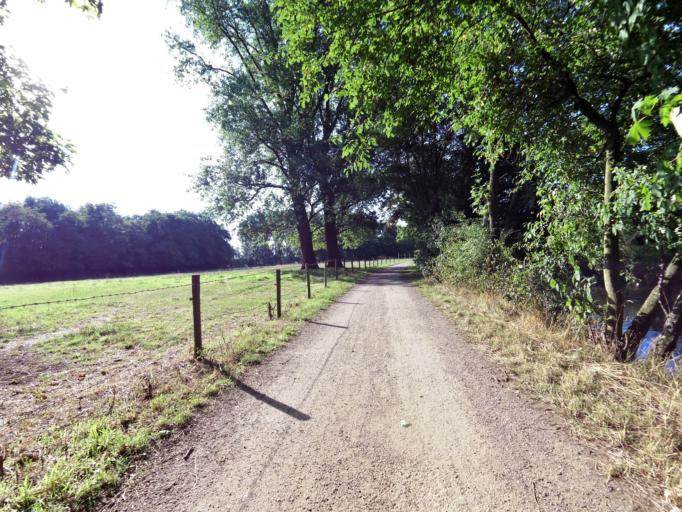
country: DE
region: North Rhine-Westphalia
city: Huckelhoven
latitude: 51.0477
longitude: 6.2084
